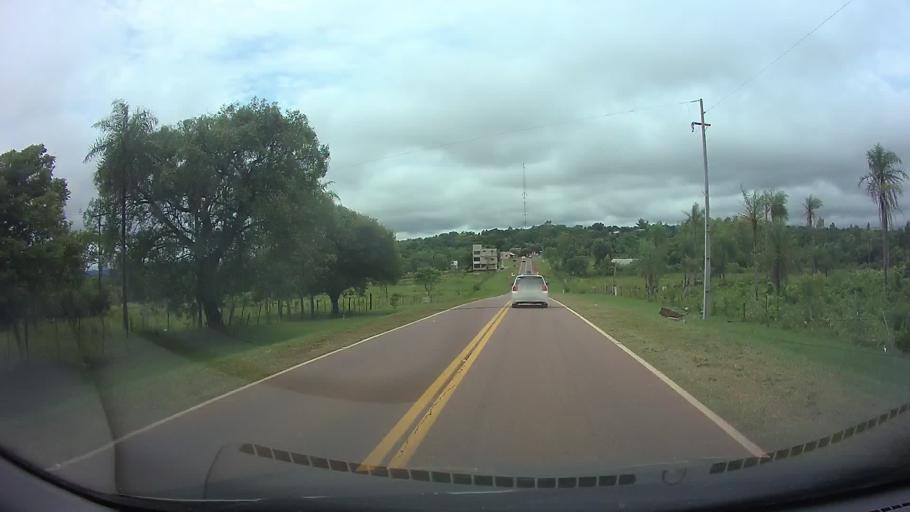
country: PY
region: Paraguari
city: Acahay
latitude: -25.9033
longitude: -57.1160
